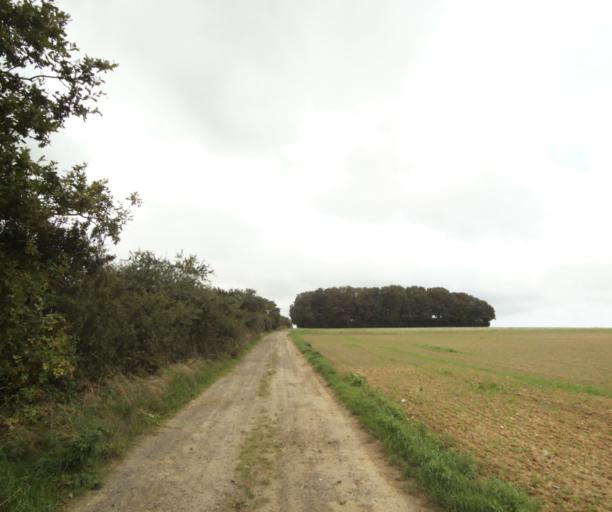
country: FR
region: Nord-Pas-de-Calais
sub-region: Departement du Pas-de-Calais
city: Etaples
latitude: 50.5288
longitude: 1.6698
